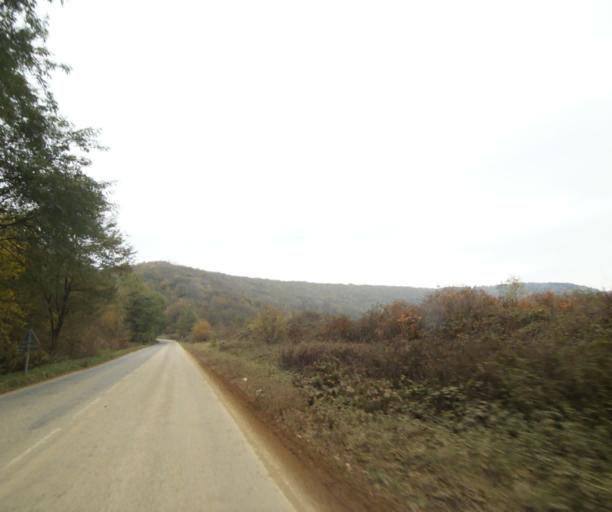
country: FR
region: Lorraine
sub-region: Departement de Meurthe-et-Moselle
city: Joeuf
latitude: 49.2404
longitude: 6.0260
